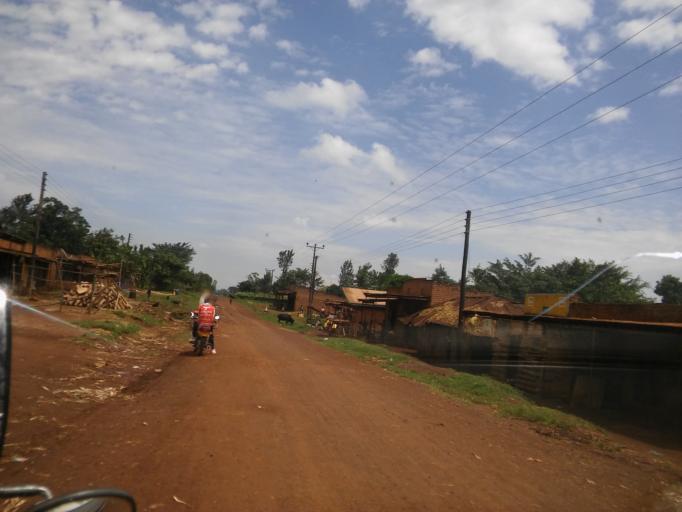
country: UG
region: Eastern Region
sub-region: Bududa District
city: Bududa
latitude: 0.8919
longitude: 34.2639
